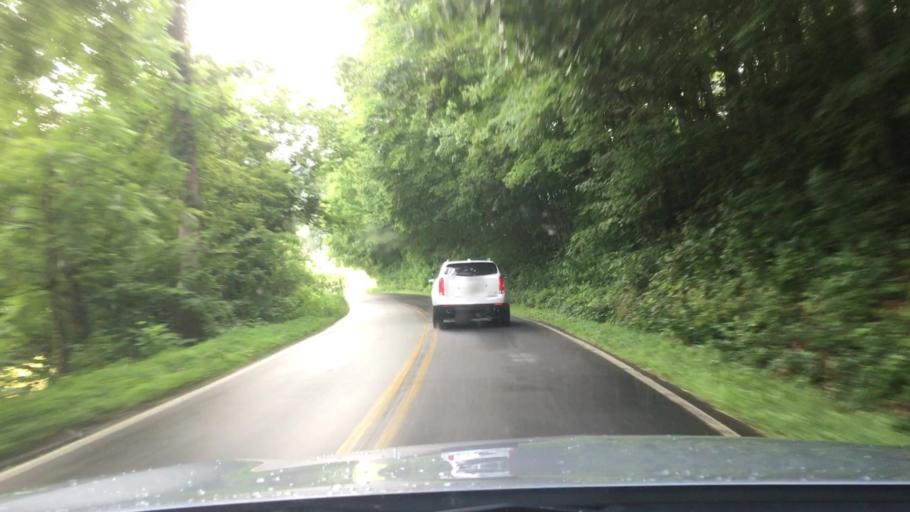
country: US
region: North Carolina
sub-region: Yancey County
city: Burnsville
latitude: 35.9061
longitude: -82.3591
